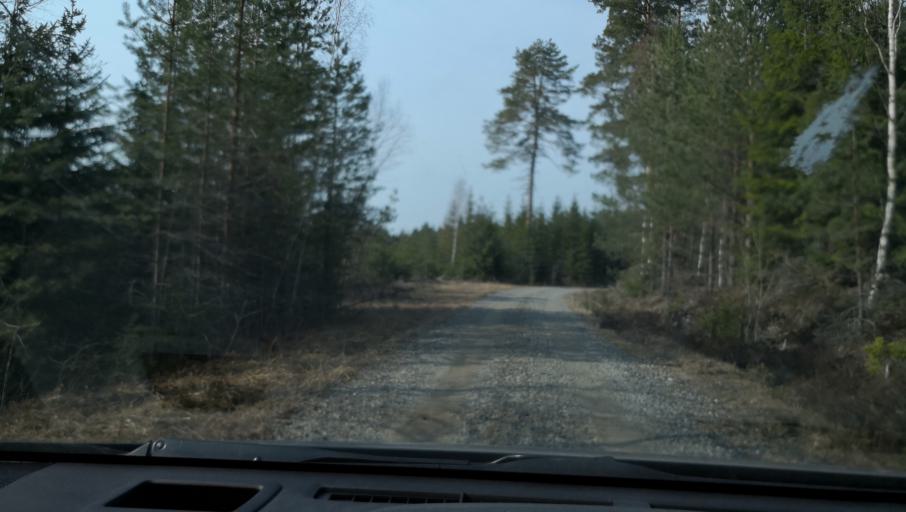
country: SE
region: OErebro
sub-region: Lindesbergs Kommun
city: Frovi
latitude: 59.3830
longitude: 15.4110
